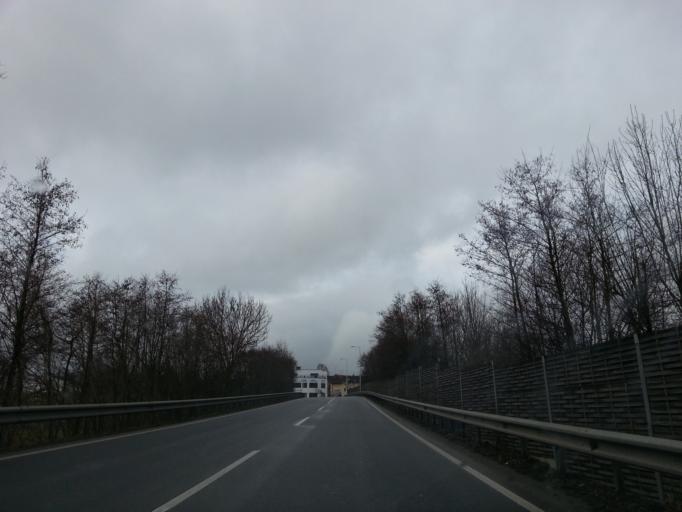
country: AT
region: Upper Austria
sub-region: Politischer Bezirk Ried im Innkreis
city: Ried im Innkreis
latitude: 48.2054
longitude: 13.4670
